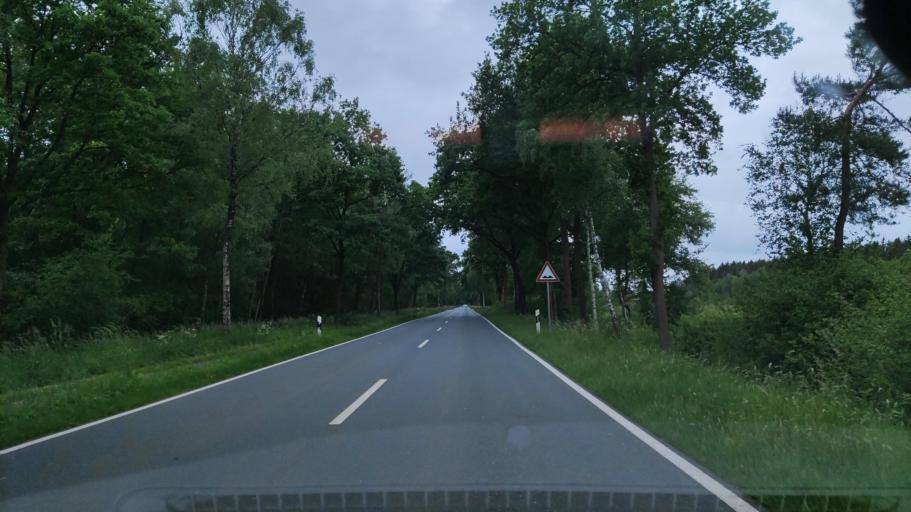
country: DE
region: Lower Saxony
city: Schneverdingen
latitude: 53.1145
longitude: 9.7380
